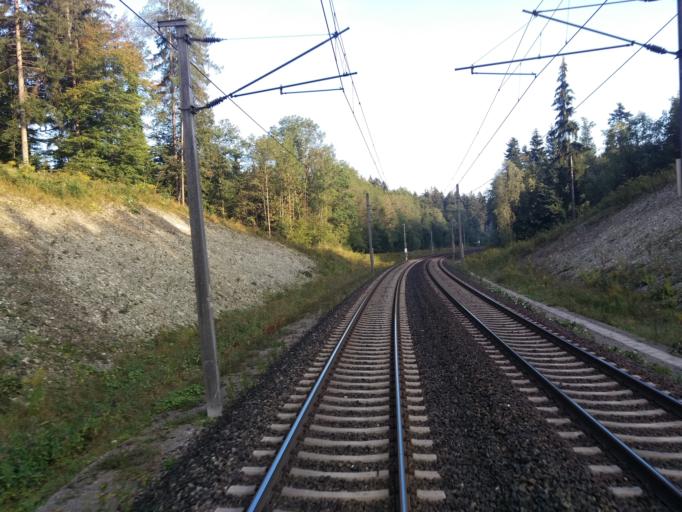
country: AT
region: Salzburg
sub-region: Politischer Bezirk Hallein
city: Adnet
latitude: 47.6589
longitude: 13.1241
